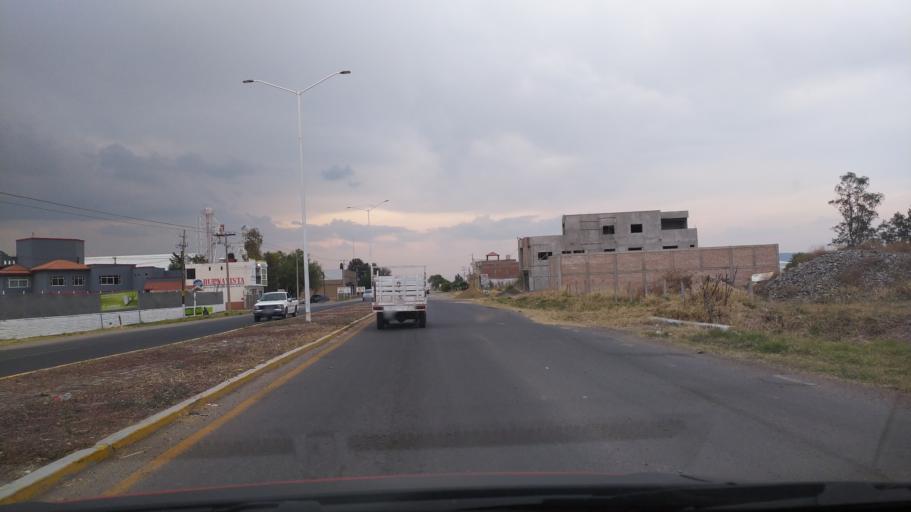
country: MX
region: Guanajuato
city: Ciudad Manuel Doblado
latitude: 20.7306
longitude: -101.9386
